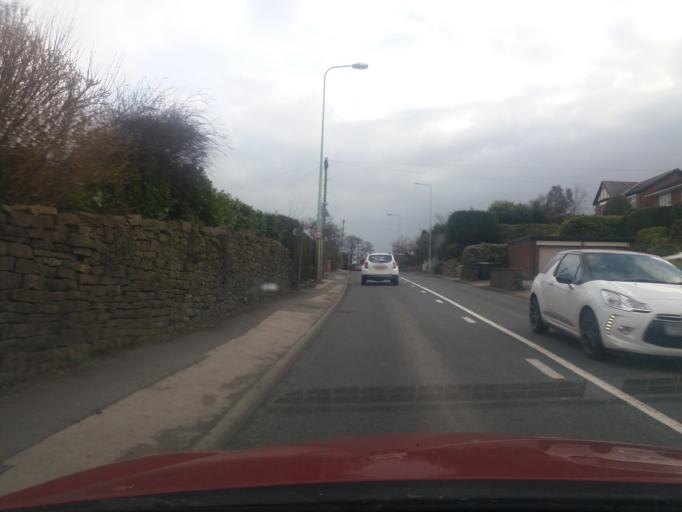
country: GB
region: England
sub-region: Lancashire
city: Chorley
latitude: 53.6782
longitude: -2.6161
